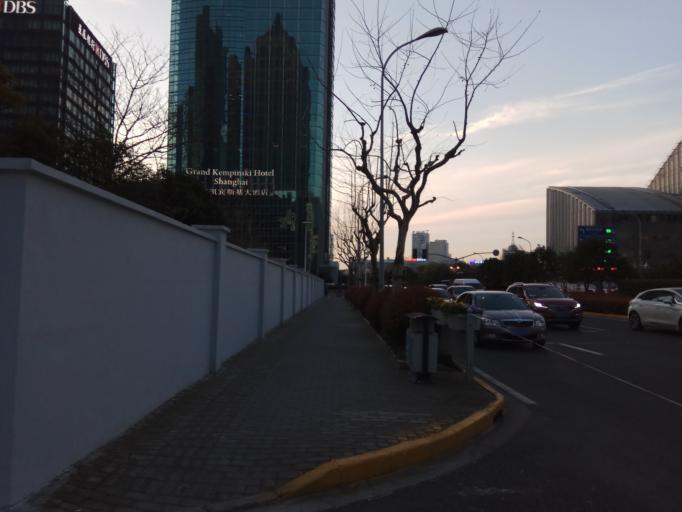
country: CN
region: Shanghai Shi
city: Hongkou
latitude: 31.2430
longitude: 121.5014
